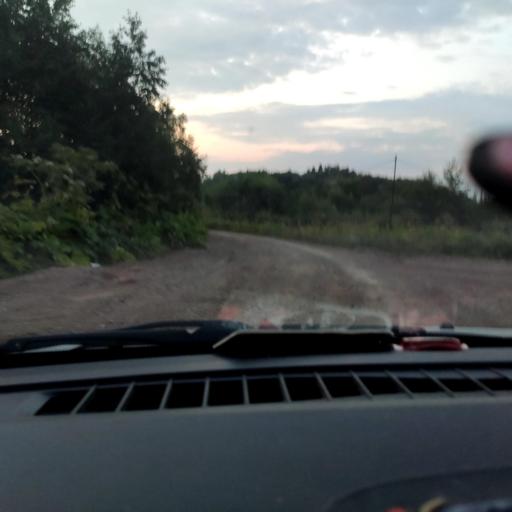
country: RU
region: Perm
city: Kultayevo
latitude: 57.8202
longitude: 55.9999
